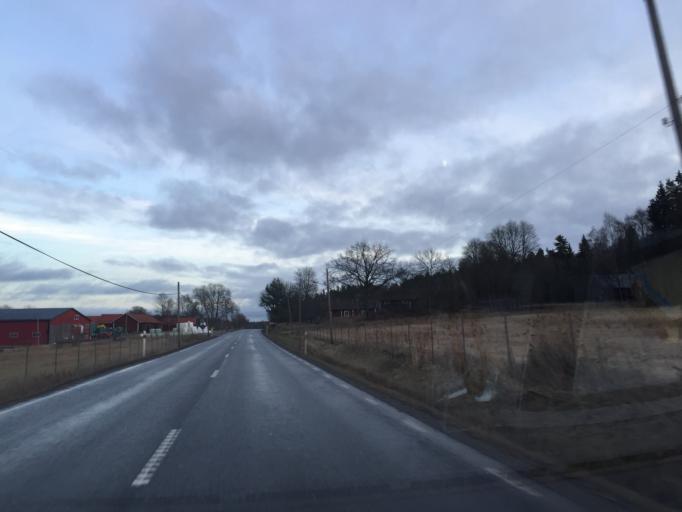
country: SE
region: Stockholm
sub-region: Salems Kommun
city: Ronninge
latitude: 59.1656
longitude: 17.7250
